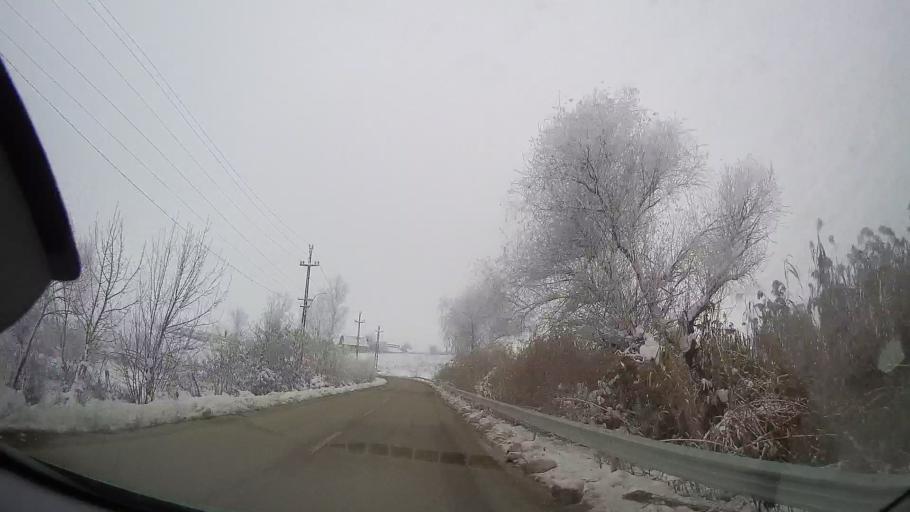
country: RO
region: Iasi
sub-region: Comuna Dagata
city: Dagata
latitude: 46.9164
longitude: 27.1974
